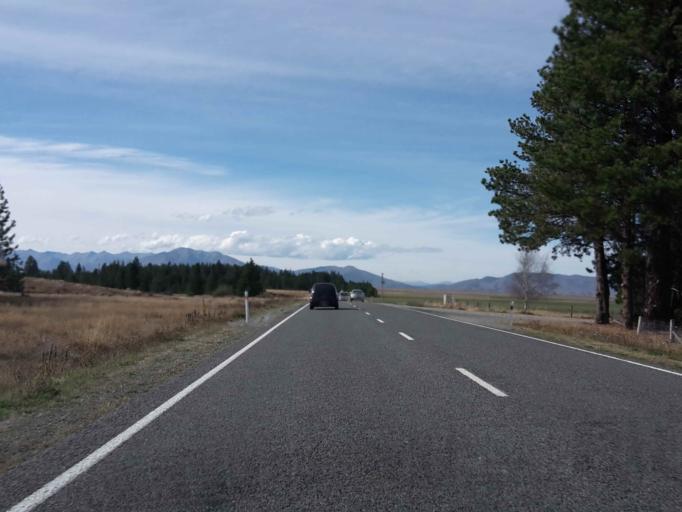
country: NZ
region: Canterbury
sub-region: Timaru District
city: Pleasant Point
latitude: -44.1849
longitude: 170.3077
